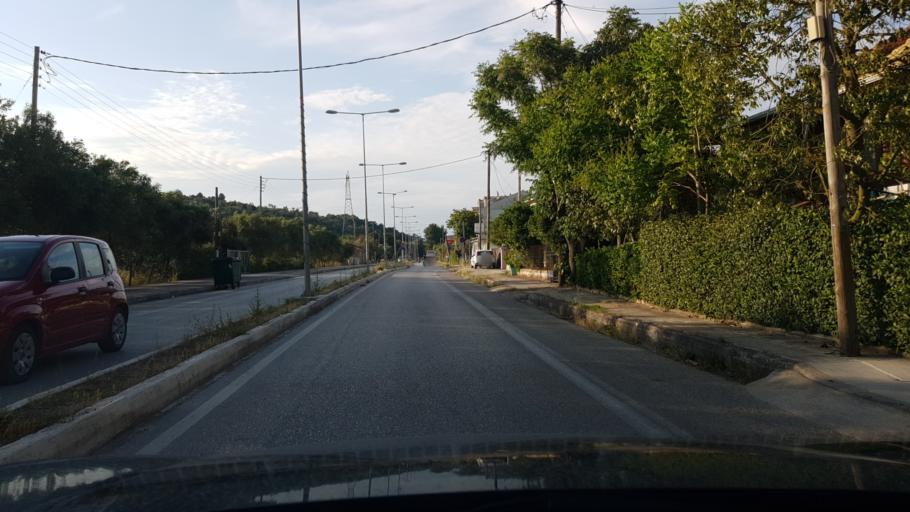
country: GR
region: Ionian Islands
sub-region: Lefkada
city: Lefkada
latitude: 38.8011
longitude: 20.7157
